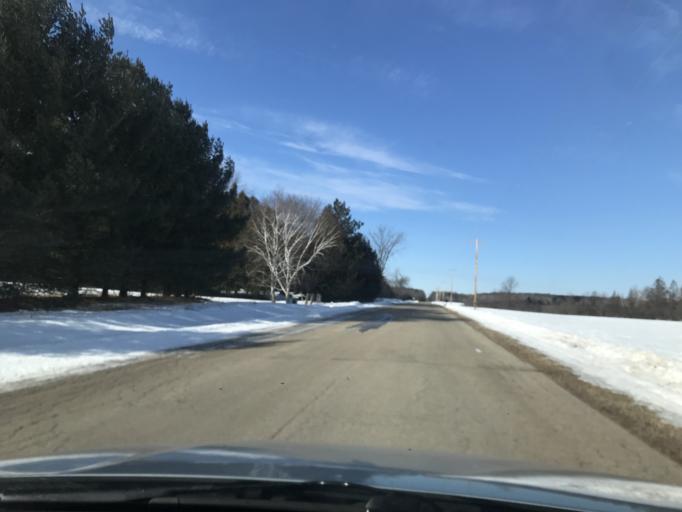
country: US
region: Wisconsin
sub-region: Oconto County
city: Gillett
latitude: 44.9614
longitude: -88.2655
